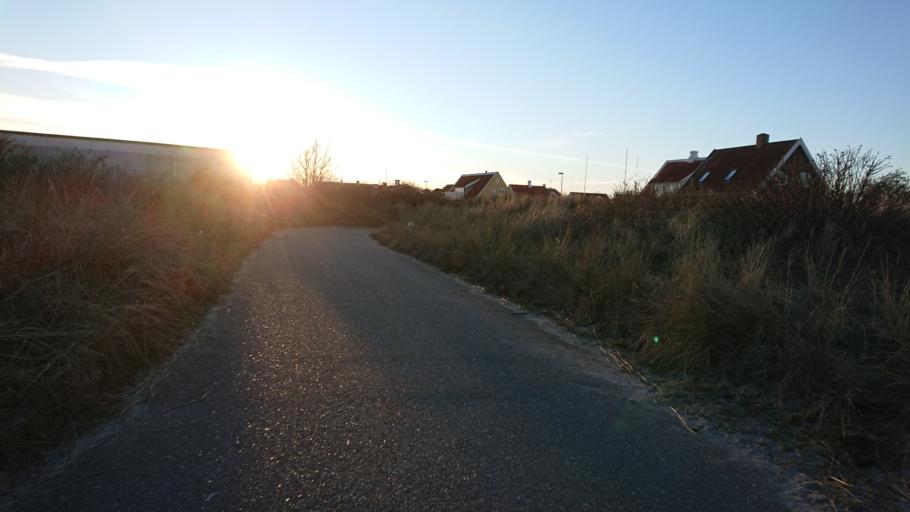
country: DK
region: North Denmark
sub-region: Frederikshavn Kommune
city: Skagen
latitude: 57.7242
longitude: 10.6033
